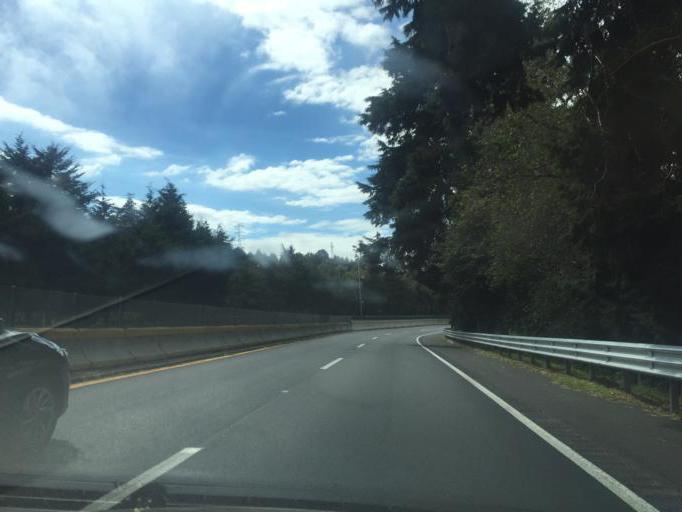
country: MX
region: Morelos
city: Tres Marias
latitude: 19.0616
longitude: -99.2388
